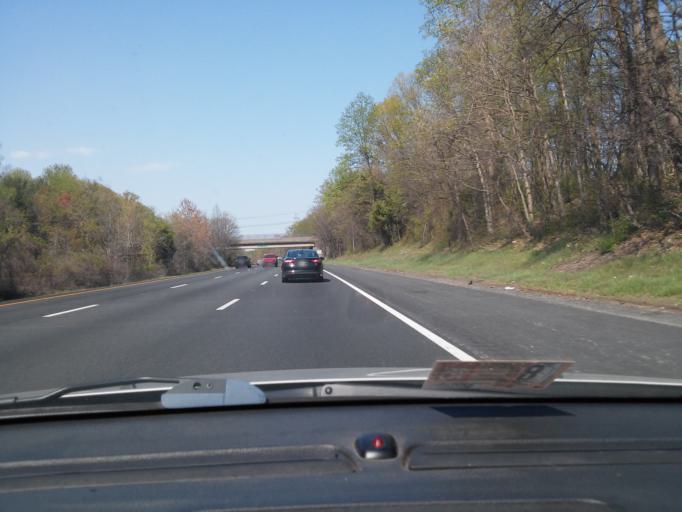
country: US
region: New Jersey
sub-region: Somerset County
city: Watchung
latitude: 40.6515
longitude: -74.4634
